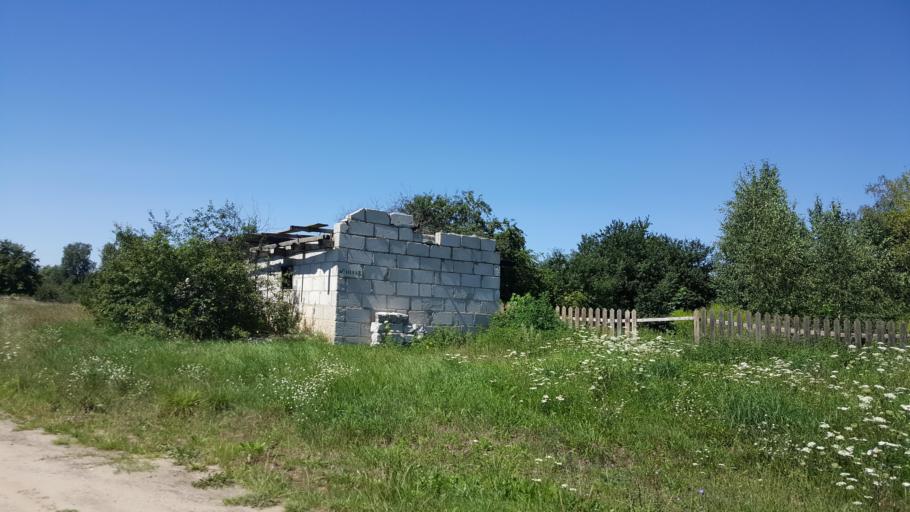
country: BY
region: Brest
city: Charnawchytsy
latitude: 52.2246
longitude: 23.7800
